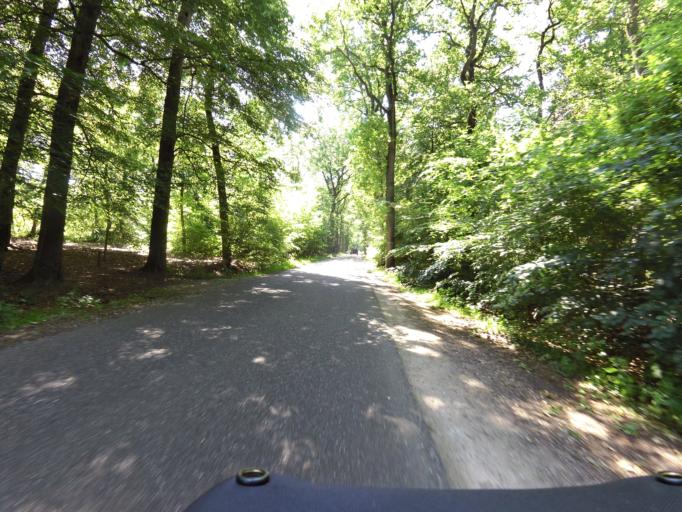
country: NL
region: Overijssel
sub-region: Gemeente Twenterand
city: Den Ham
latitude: 52.5169
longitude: 6.4907
